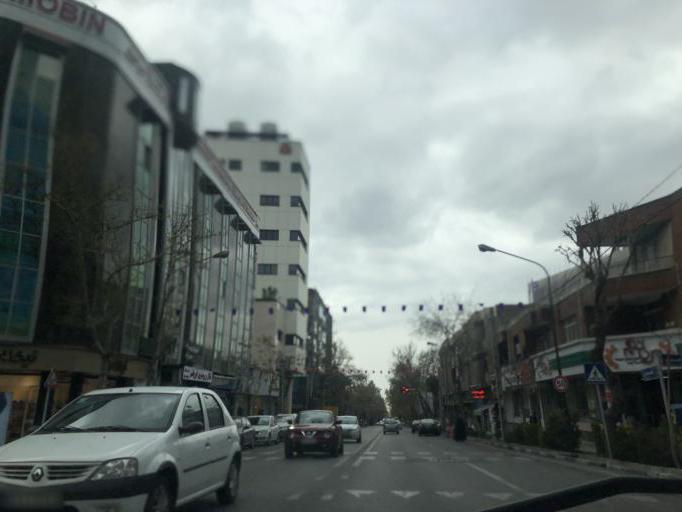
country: IR
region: Tehran
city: Tajrish
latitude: 35.7744
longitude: 51.4635
